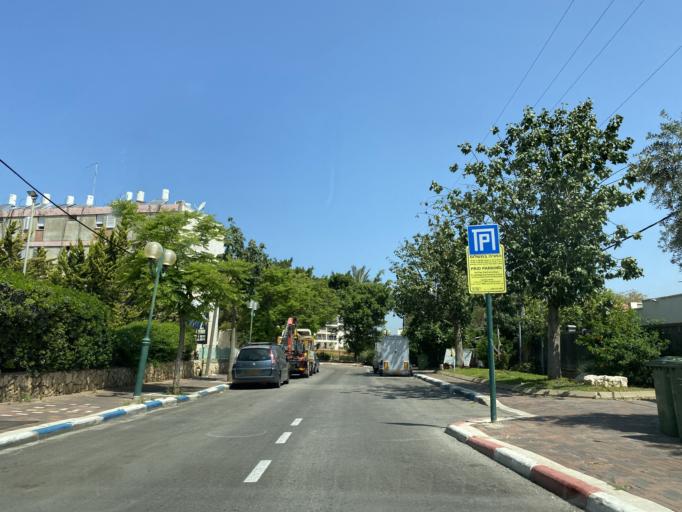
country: IL
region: Central District
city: Ra'anana
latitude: 32.1918
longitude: 34.8719
